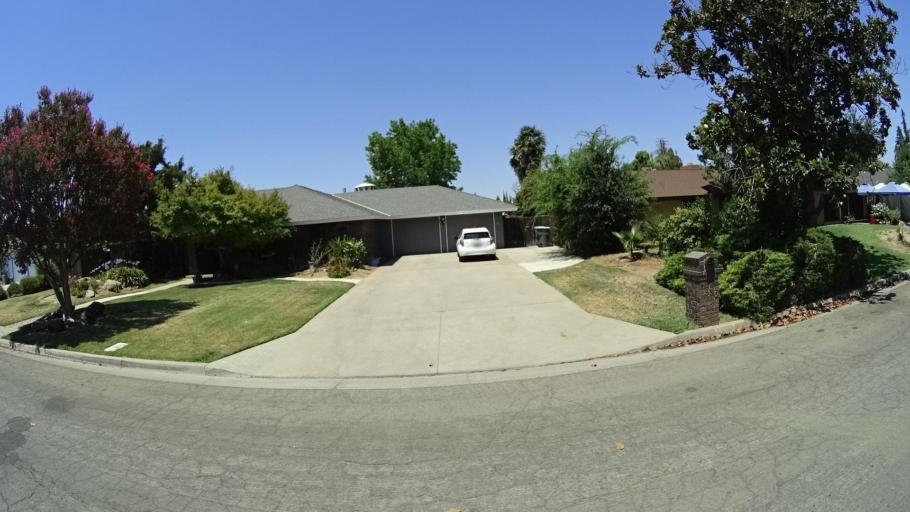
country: US
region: California
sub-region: Fresno County
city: Sunnyside
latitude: 36.7266
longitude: -119.7245
